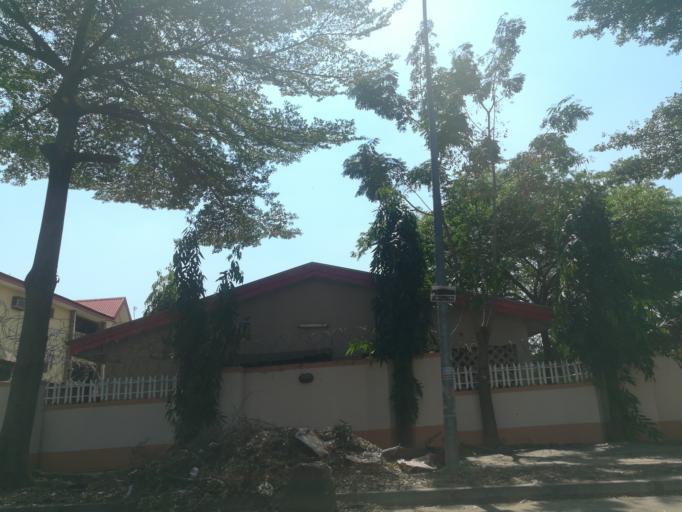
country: NG
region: Abuja Federal Capital Territory
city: Abuja
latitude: 9.0683
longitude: 7.4495
